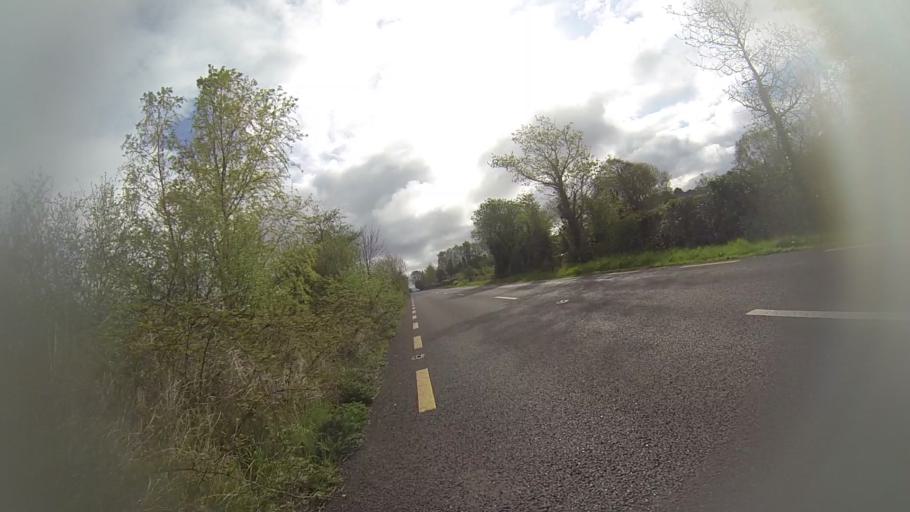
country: IE
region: Munster
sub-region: Ciarrai
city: Kenmare
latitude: 51.8814
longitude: -9.6057
